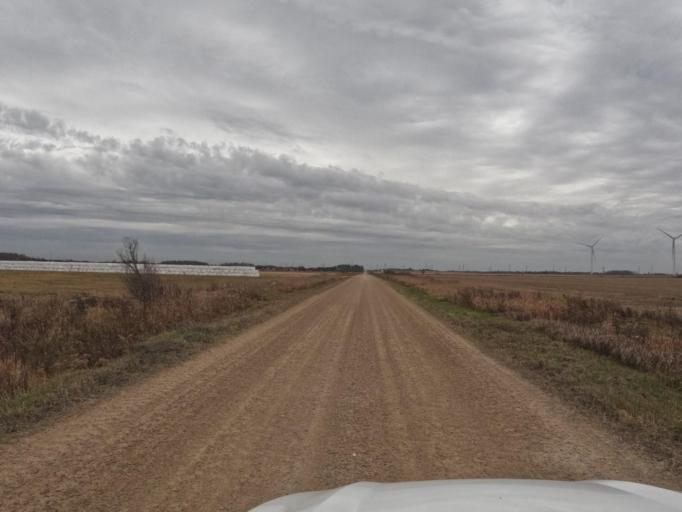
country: CA
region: Ontario
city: Shelburne
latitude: 44.0183
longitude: -80.3913
